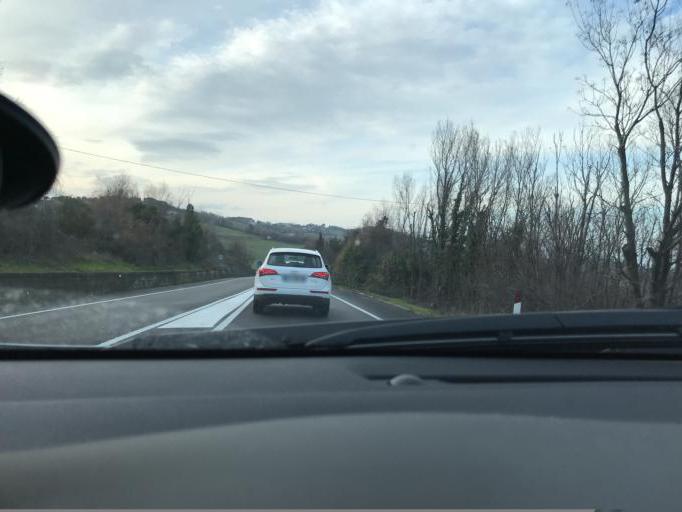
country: IT
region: The Marches
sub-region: Provincia di Ancona
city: Posatora
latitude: 43.6013
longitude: 13.4321
